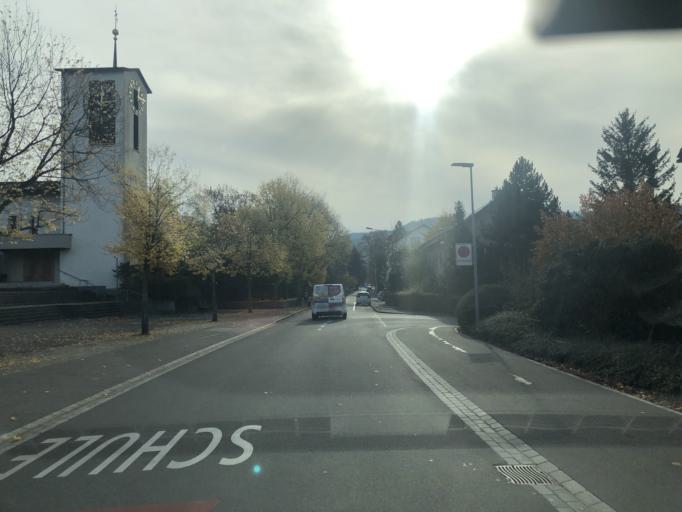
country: CH
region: Aargau
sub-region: Bezirk Baden
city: Wettingen
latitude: 47.4635
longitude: 8.3183
